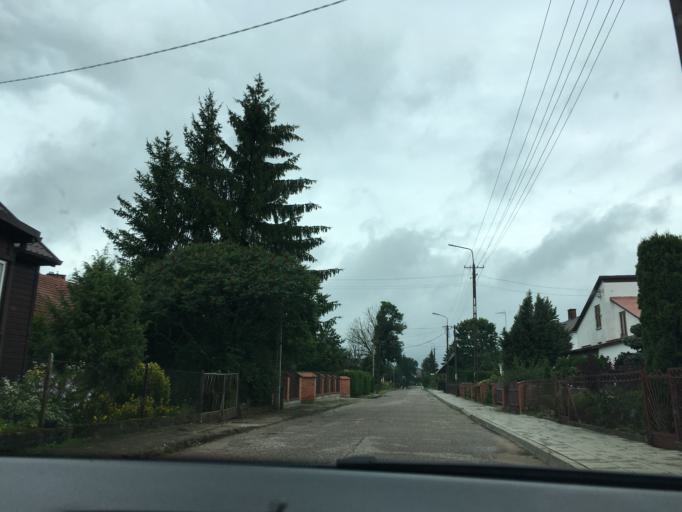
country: PL
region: Podlasie
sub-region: Powiat sejnenski
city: Krasnopol
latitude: 54.1178
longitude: 23.2051
